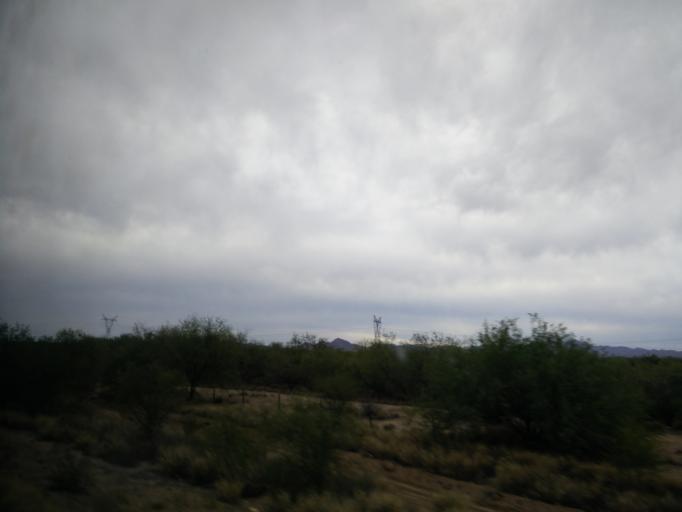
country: MX
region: Sonora
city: Hermosillo
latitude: 28.6613
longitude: -111.0007
